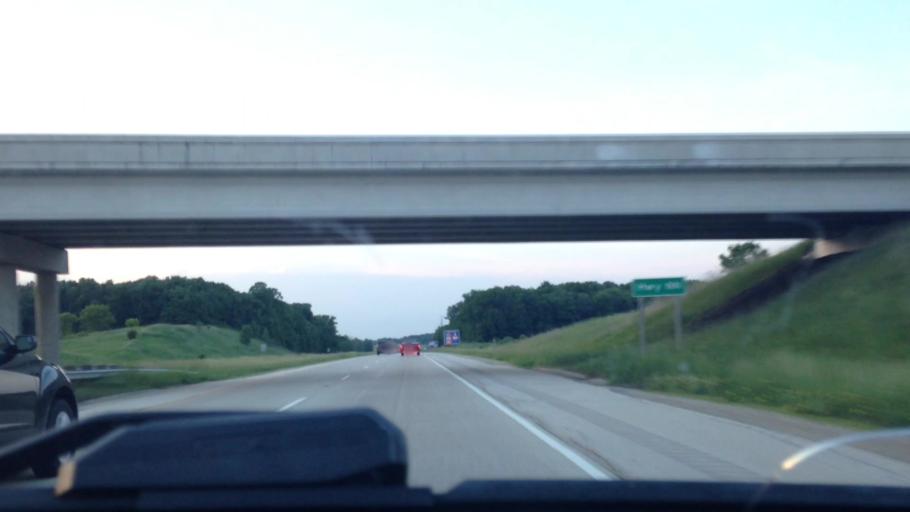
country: US
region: Wisconsin
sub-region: Washington County
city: West Bend
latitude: 43.3830
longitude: -88.1927
